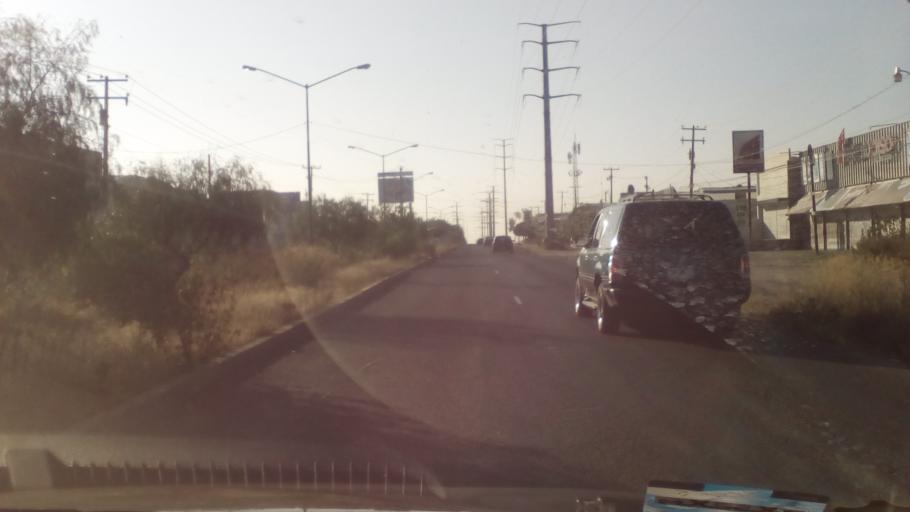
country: MX
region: Guanajuato
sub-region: Leon
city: La Ermita
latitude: 21.1479
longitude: -101.7280
